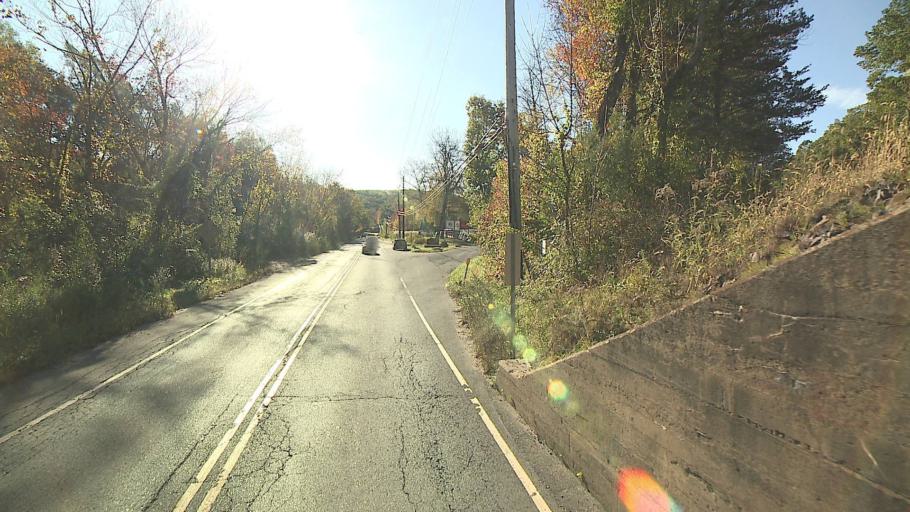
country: US
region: Connecticut
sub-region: Fairfield County
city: Bethel
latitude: 41.3573
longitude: -73.4183
